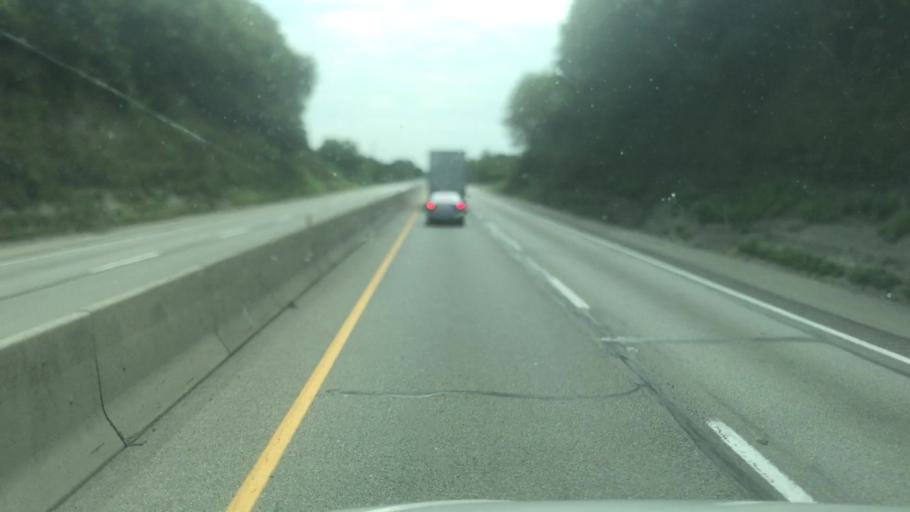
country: US
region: Pennsylvania
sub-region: Beaver County
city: Freedom
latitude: 40.7519
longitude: -80.2112
